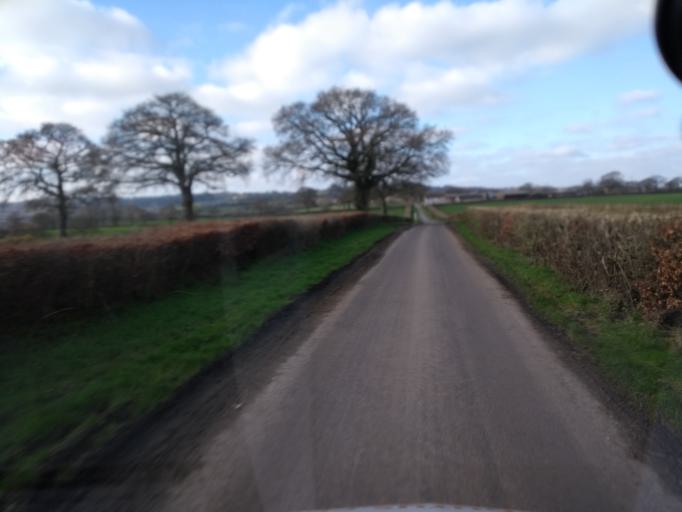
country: GB
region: England
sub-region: Somerset
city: Chard
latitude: 50.9334
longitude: -2.9915
